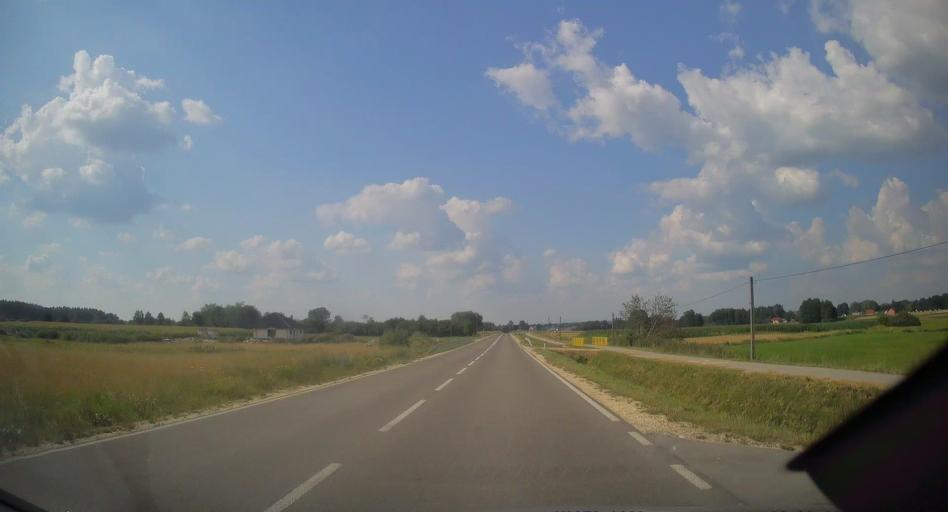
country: PL
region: Swietokrzyskie
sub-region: Powiat kielecki
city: Lopuszno
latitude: 50.9592
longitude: 20.2485
